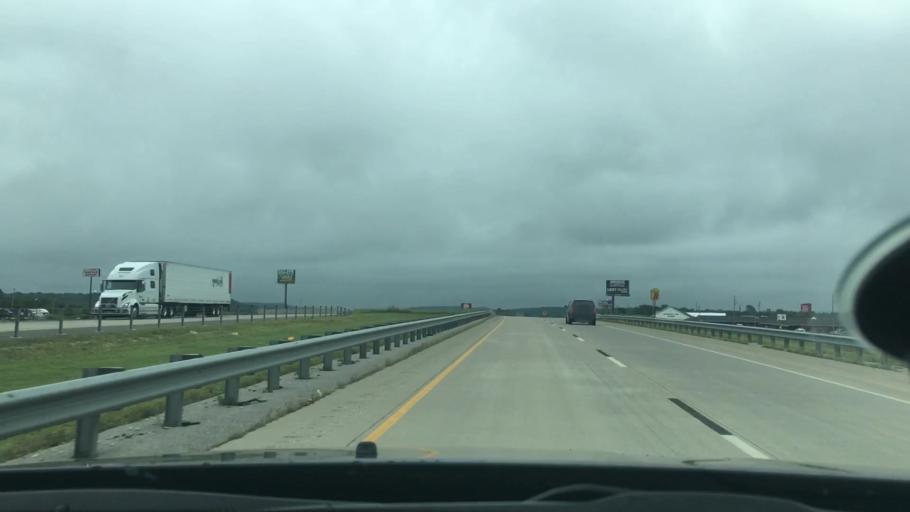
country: US
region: Oklahoma
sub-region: Okmulgee County
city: Henryetta
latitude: 35.4328
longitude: -96.0183
